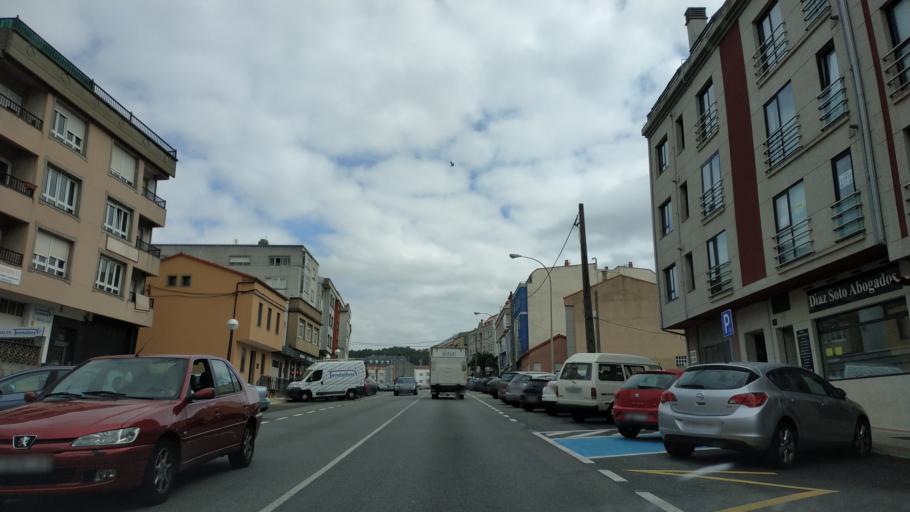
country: ES
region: Galicia
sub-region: Provincia da Coruna
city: Arteixo
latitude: 43.3170
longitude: -8.4840
